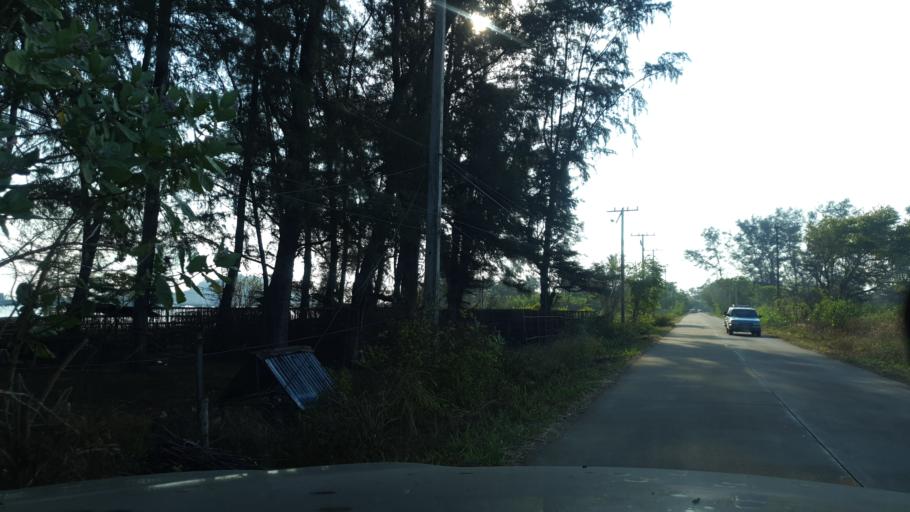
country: TH
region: Prachuap Khiri Khan
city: Bang Saphan
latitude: 11.2196
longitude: 99.5684
